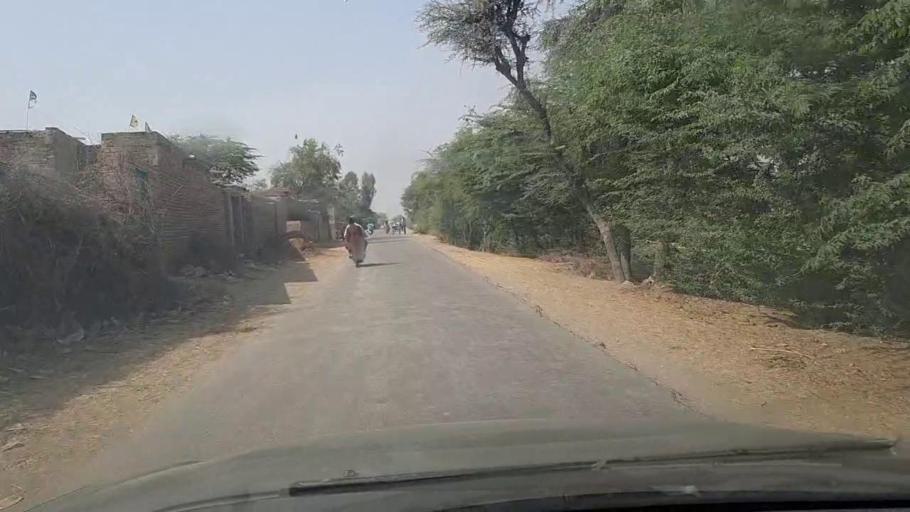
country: PK
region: Sindh
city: Mirpur Mathelo
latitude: 27.9289
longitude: 69.5329
